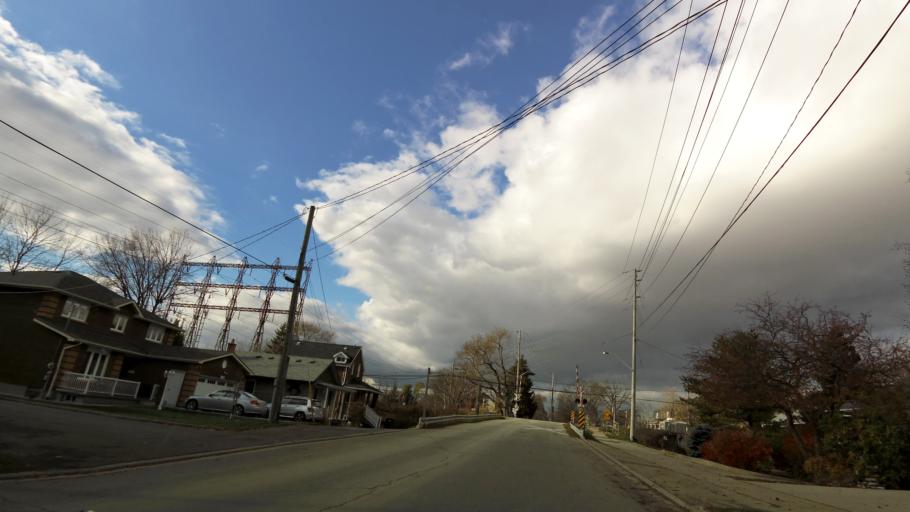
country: CA
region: Ontario
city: Etobicoke
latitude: 43.5816
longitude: -79.5582
